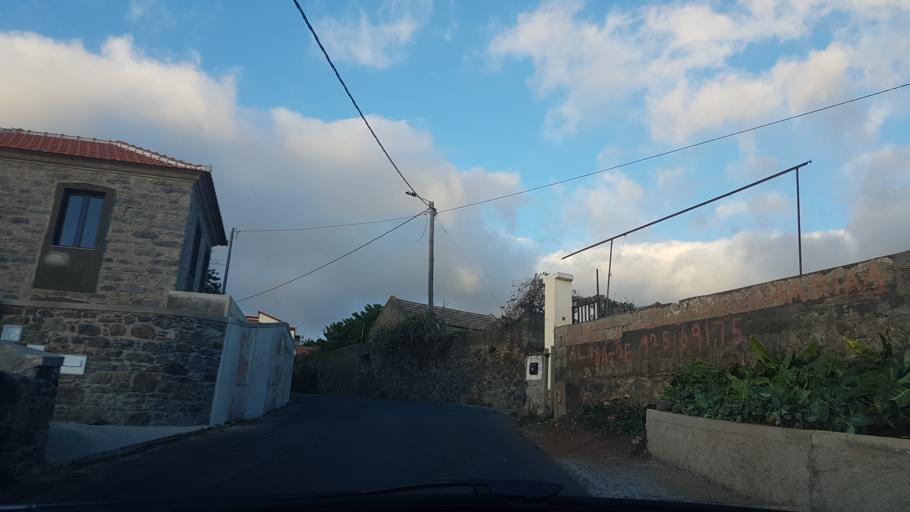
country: PT
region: Madeira
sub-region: Calheta
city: Arco da Calheta
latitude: 32.7015
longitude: -17.1246
